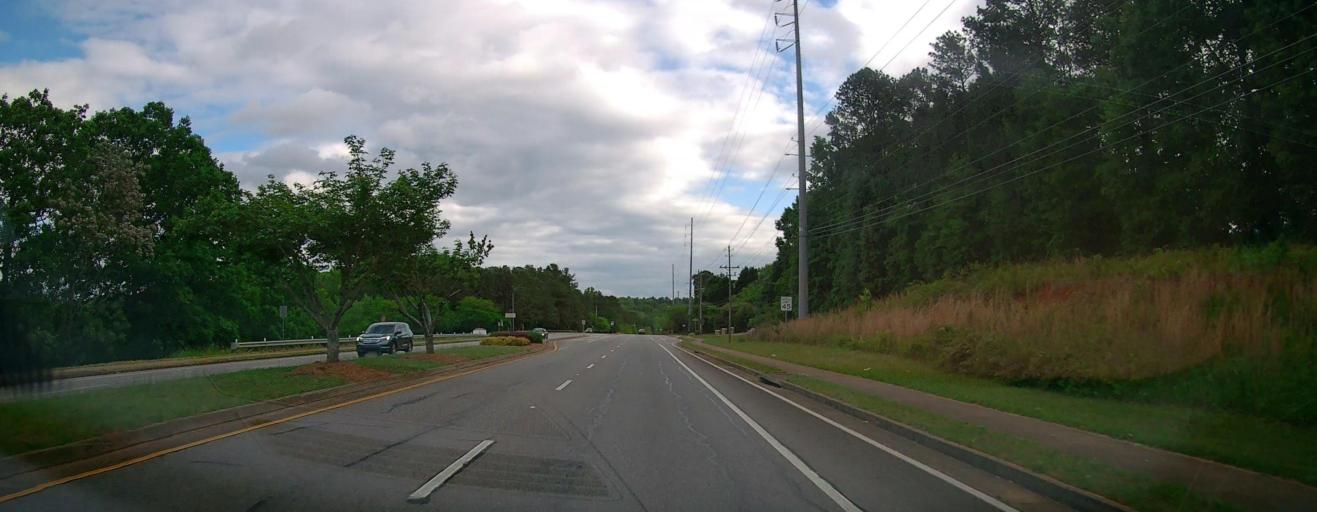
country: US
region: Georgia
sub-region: Clarke County
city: Country Club Estates
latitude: 33.9299
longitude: -83.4384
